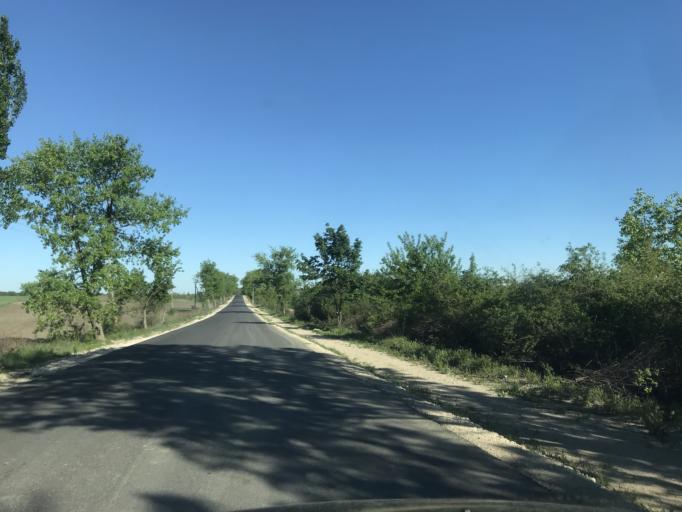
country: MD
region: Chisinau
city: Cricova
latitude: 47.2495
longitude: 28.8170
